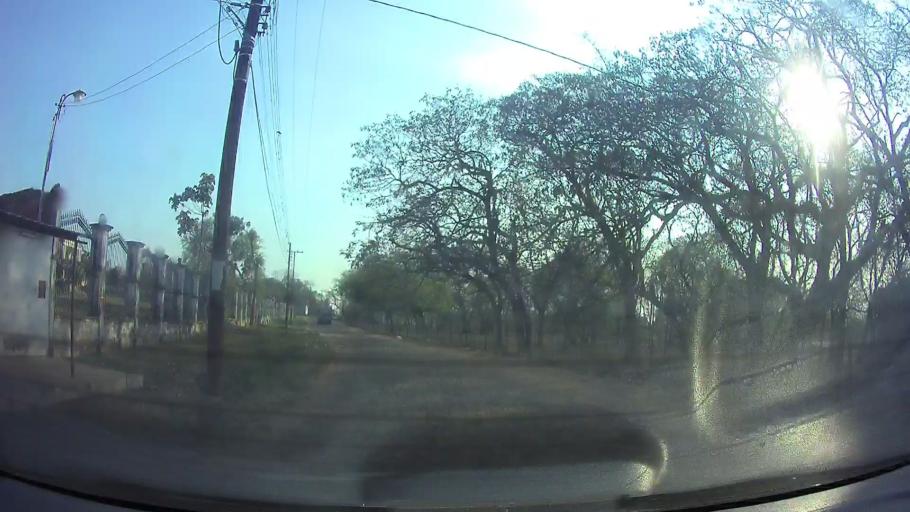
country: PY
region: Central
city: Limpio
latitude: -25.2203
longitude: -57.5037
